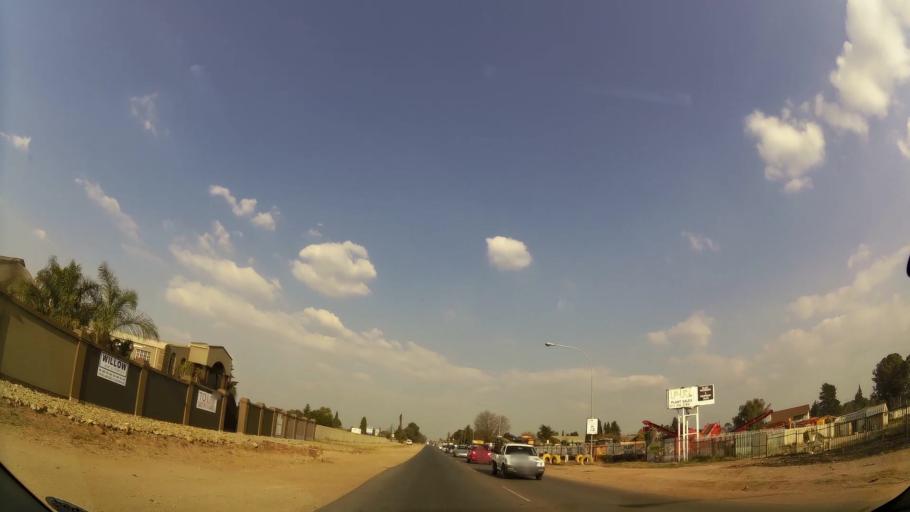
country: ZA
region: Gauteng
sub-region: Ekurhuleni Metropolitan Municipality
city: Tembisa
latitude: -26.0829
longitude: 28.2881
